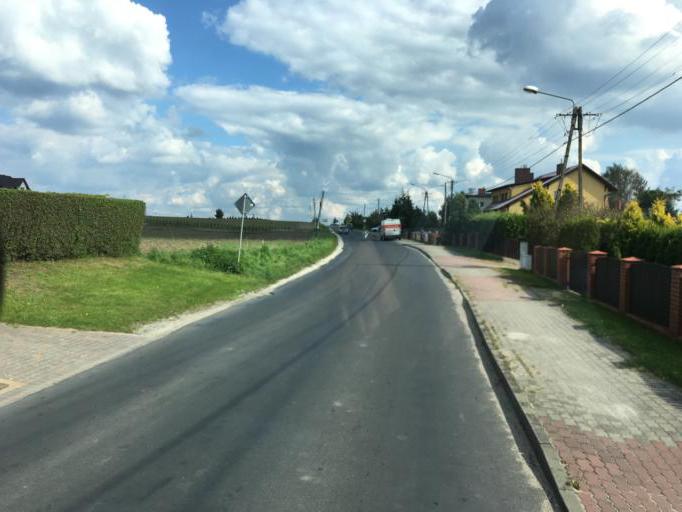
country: PL
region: Kujawsko-Pomorskie
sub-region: Powiat tucholski
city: Tuchola
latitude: 53.5928
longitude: 17.8695
